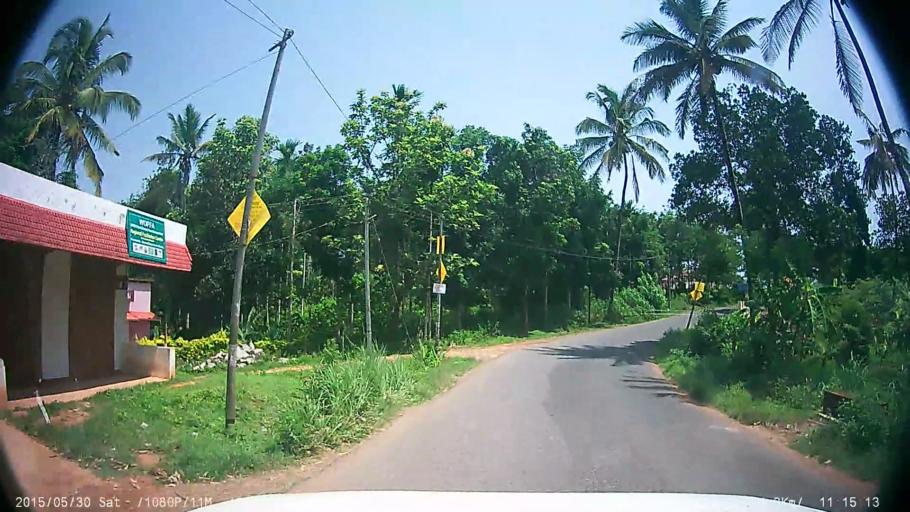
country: IN
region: Kerala
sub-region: Wayanad
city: Panamaram
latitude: 11.7691
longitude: 76.0610
